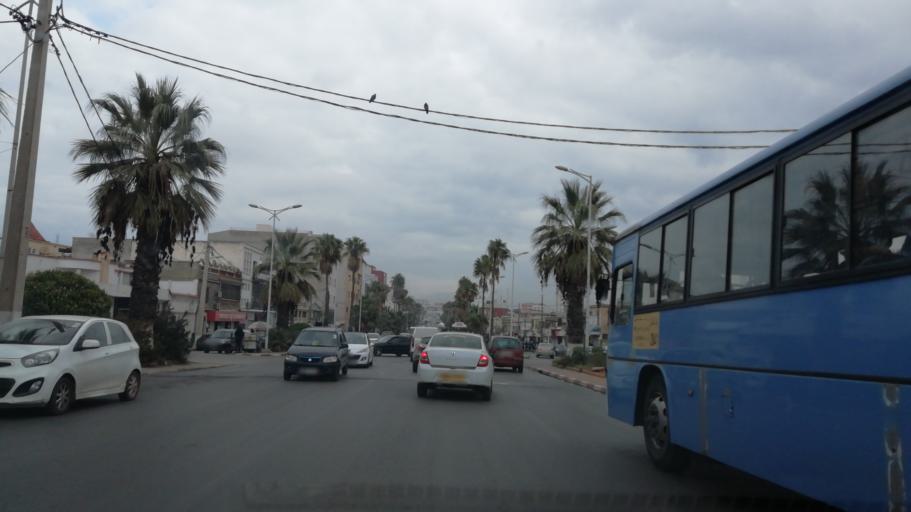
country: DZ
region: Oran
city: Oran
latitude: 35.6924
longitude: -0.6185
